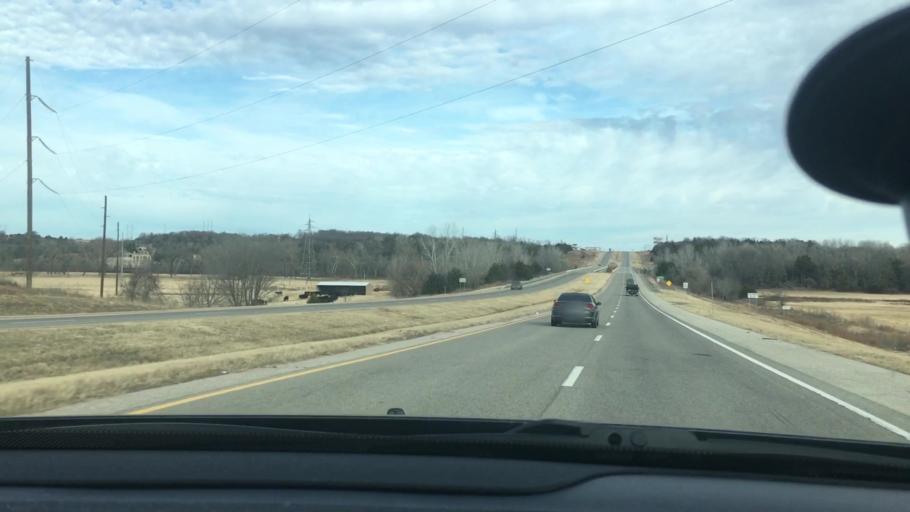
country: US
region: Oklahoma
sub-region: Pontotoc County
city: Byng
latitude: 34.9274
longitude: -96.6838
